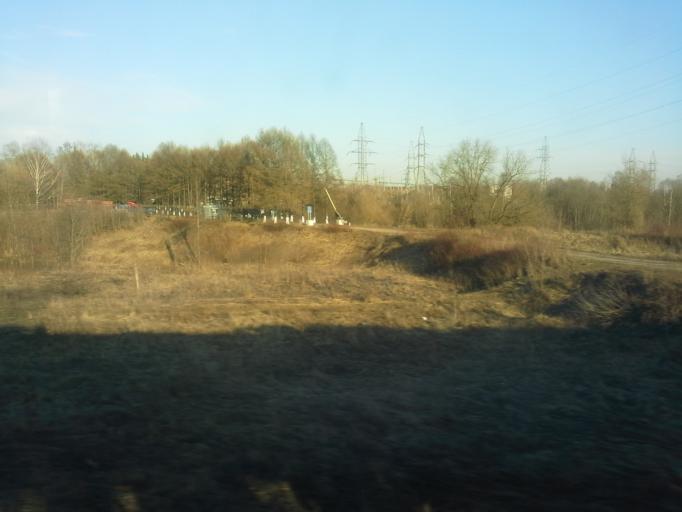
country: RU
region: Moskovskaya
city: Iksha
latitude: 56.1621
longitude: 37.5018
